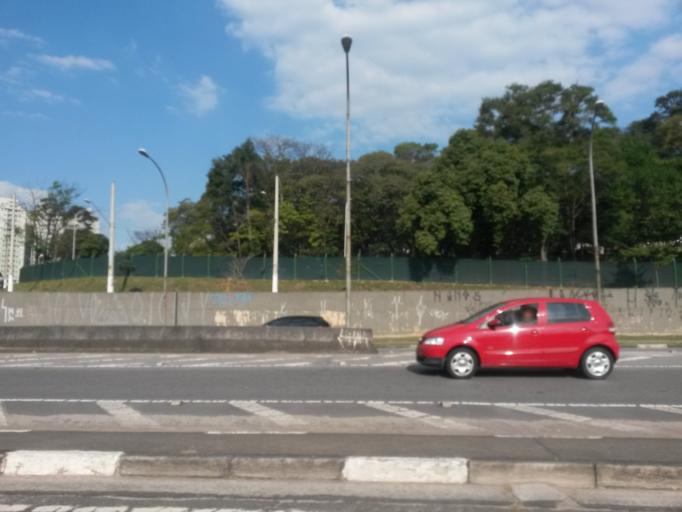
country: BR
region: Sao Paulo
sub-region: Sao Bernardo Do Campo
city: Sao Bernardo do Campo
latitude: -23.7100
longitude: -46.5636
